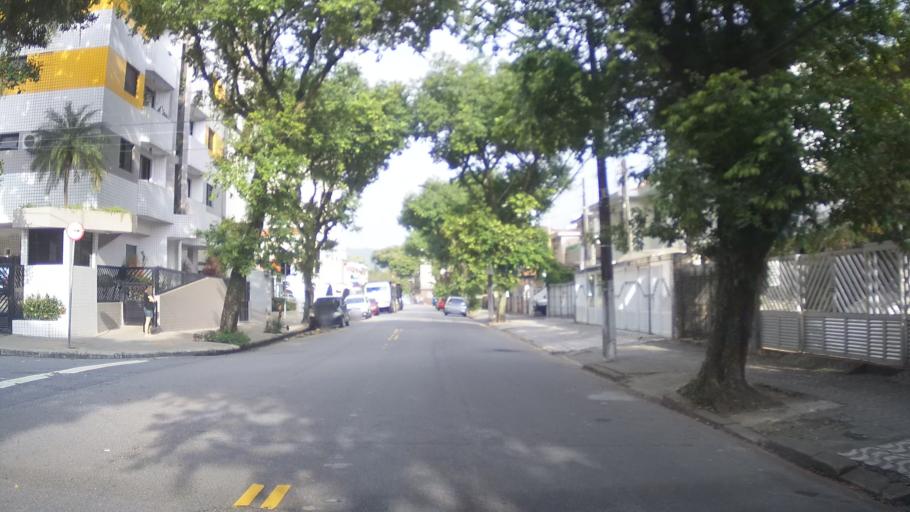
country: BR
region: Sao Paulo
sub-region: Santos
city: Santos
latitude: -23.9580
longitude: -46.3246
